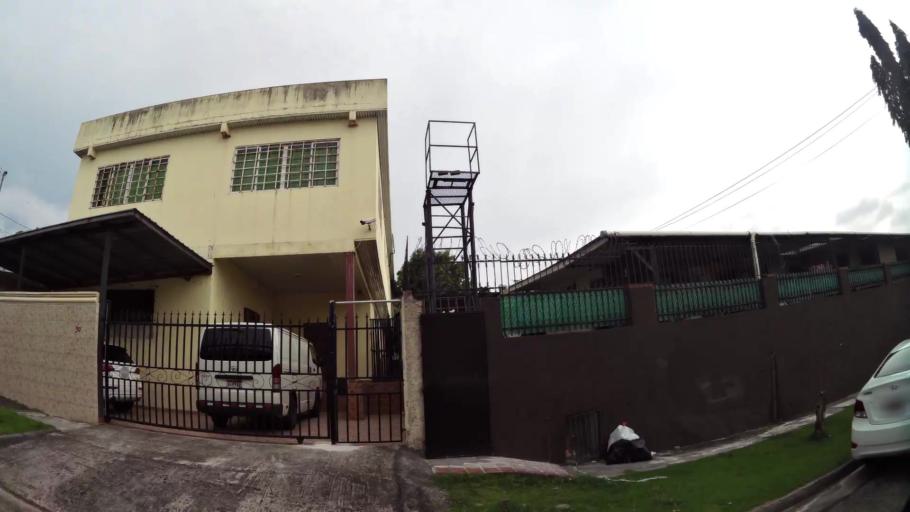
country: PA
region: Panama
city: Panama
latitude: 9.0088
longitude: -79.5332
